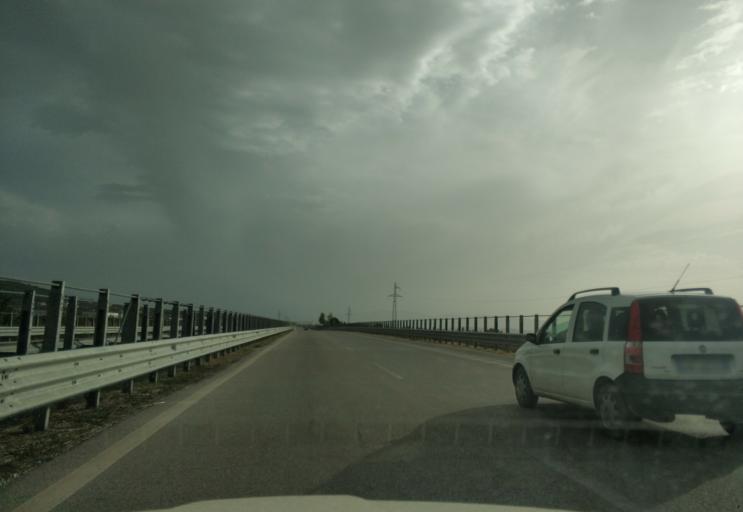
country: AL
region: Vlore
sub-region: Rrethi i Vlores
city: Novosele
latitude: 40.5883
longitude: 19.4746
